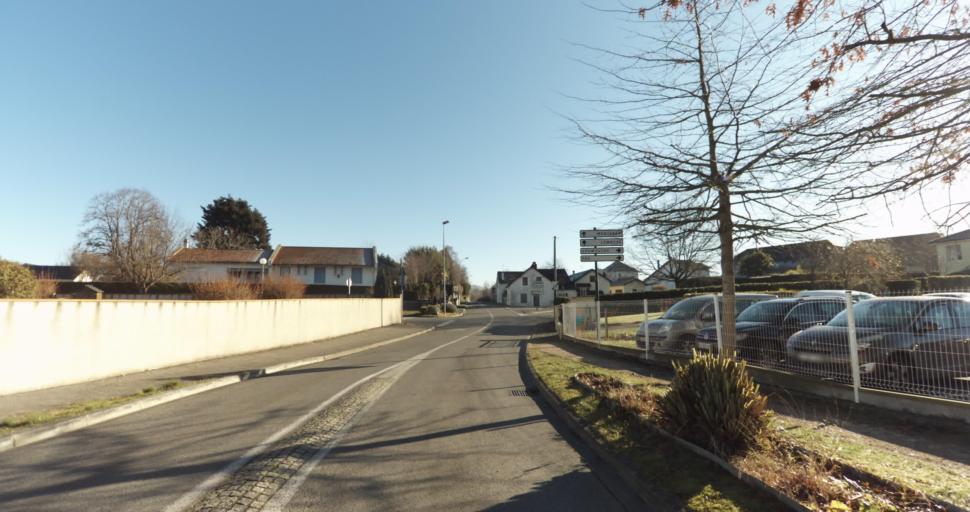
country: FR
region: Aquitaine
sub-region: Departement des Pyrenees-Atlantiques
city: Morlaas
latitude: 43.3429
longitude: -0.2587
